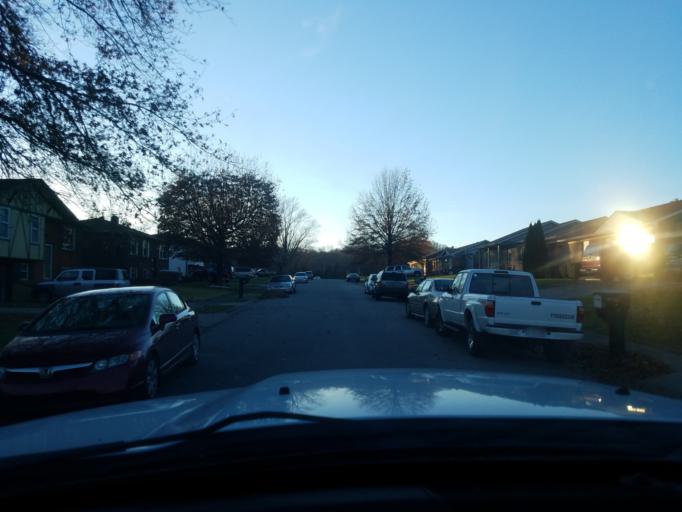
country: US
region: Indiana
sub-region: Floyd County
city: New Albany
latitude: 38.3236
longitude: -85.8334
